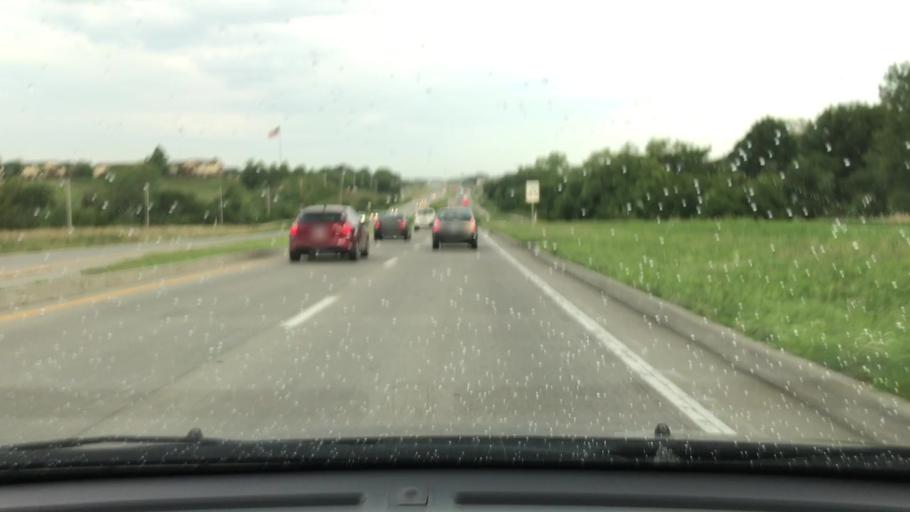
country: US
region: Missouri
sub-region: Jackson County
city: Grandview
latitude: 38.8575
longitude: -94.5107
